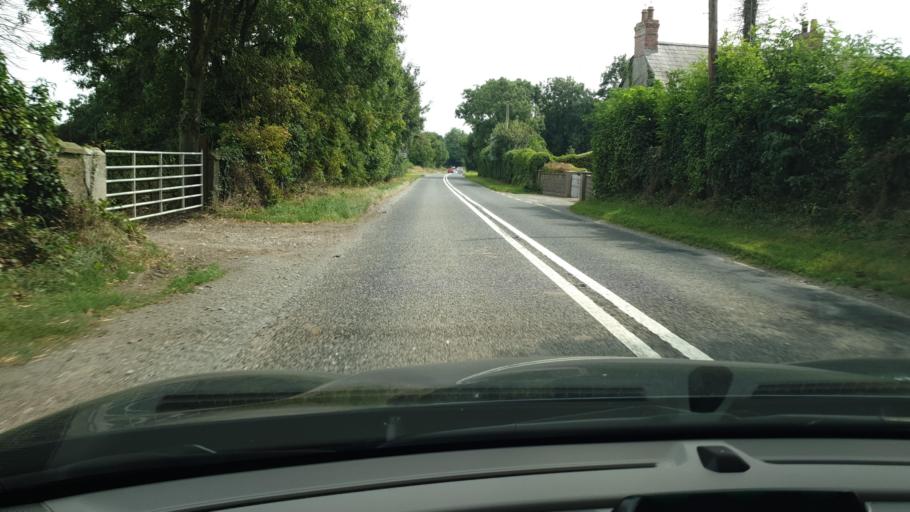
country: IE
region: Leinster
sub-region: An Mhi
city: Kells
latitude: 53.7127
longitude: -6.8216
